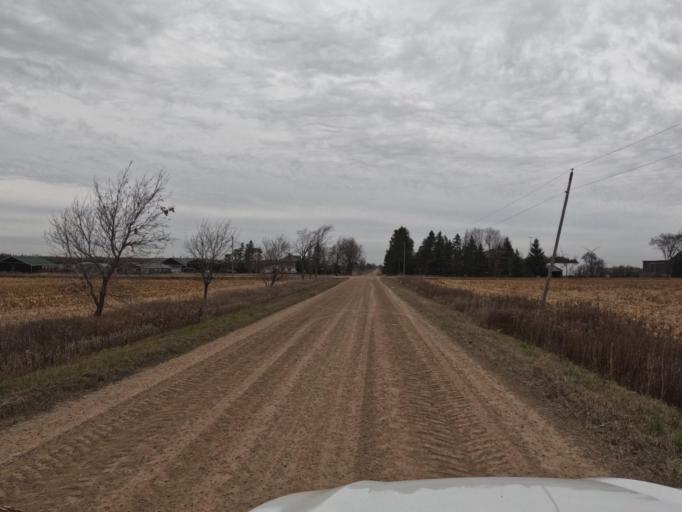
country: CA
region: Ontario
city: Shelburne
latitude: 44.0143
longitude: -80.3676
